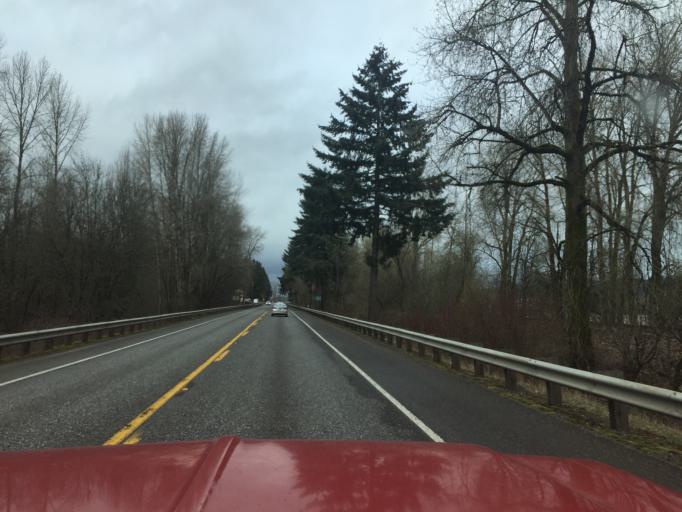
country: US
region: Washington
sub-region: Cowlitz County
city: Kalama
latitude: 46.0110
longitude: -122.8748
